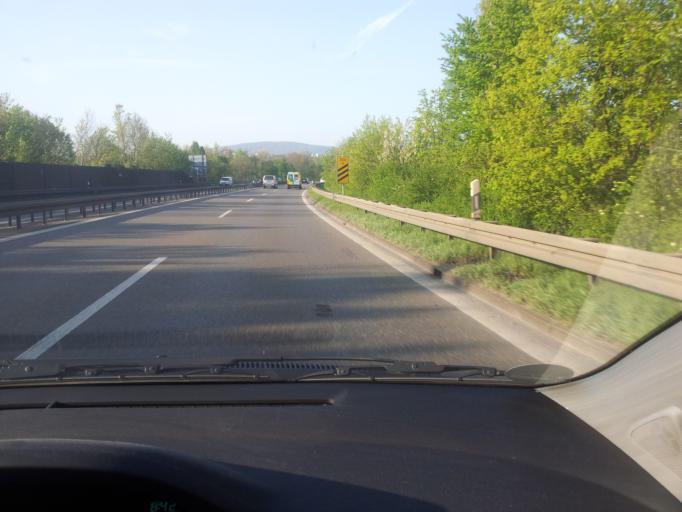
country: DE
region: Baden-Wuerttemberg
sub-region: Regierungsbezirk Stuttgart
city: Waiblingen
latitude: 48.8231
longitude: 9.3331
